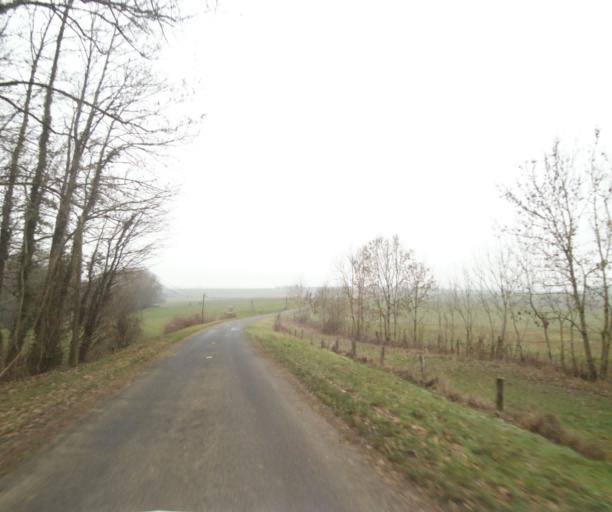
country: FR
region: Champagne-Ardenne
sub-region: Departement de la Haute-Marne
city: Bienville
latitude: 48.5079
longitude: 5.0285
